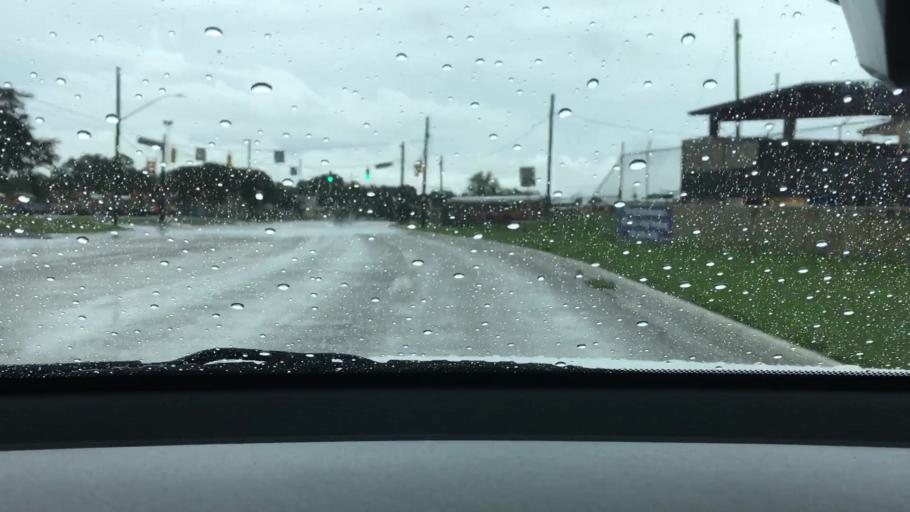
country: US
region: Texas
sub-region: Bexar County
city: Alamo Heights
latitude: 29.5371
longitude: -98.4486
